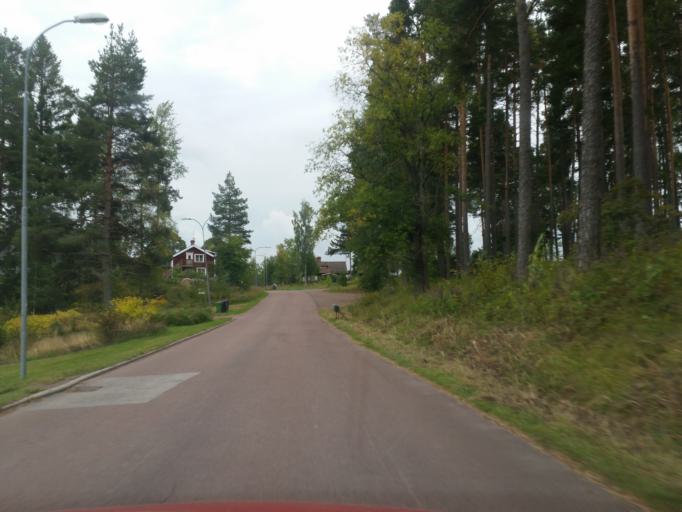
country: SE
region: Dalarna
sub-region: Leksand Municipality
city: Smedby
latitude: 60.6765
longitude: 15.1039
